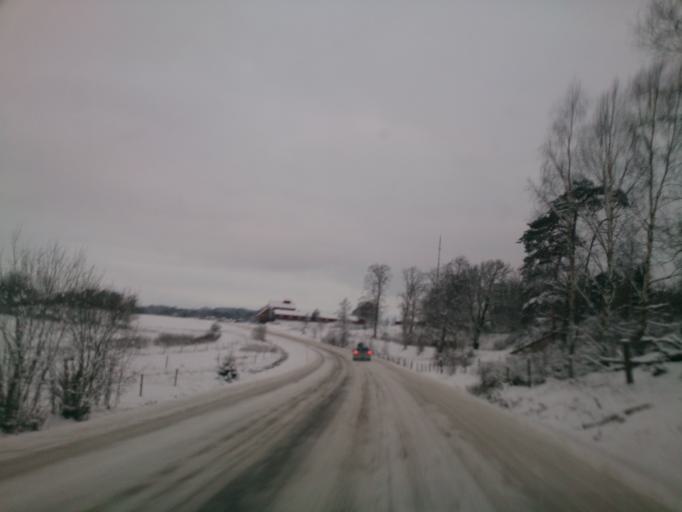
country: SE
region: OEstergoetland
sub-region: Norrkopings Kommun
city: Kimstad
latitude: 58.4068
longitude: 15.9388
